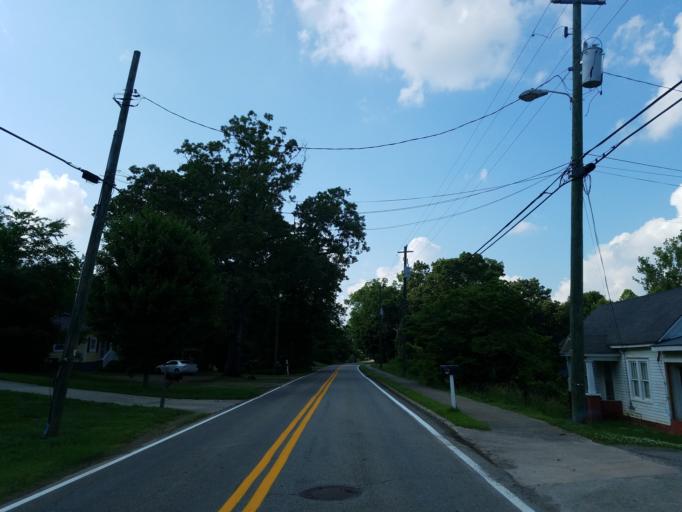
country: US
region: Georgia
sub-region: Cherokee County
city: Ball Ground
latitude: 34.3425
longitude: -84.3775
